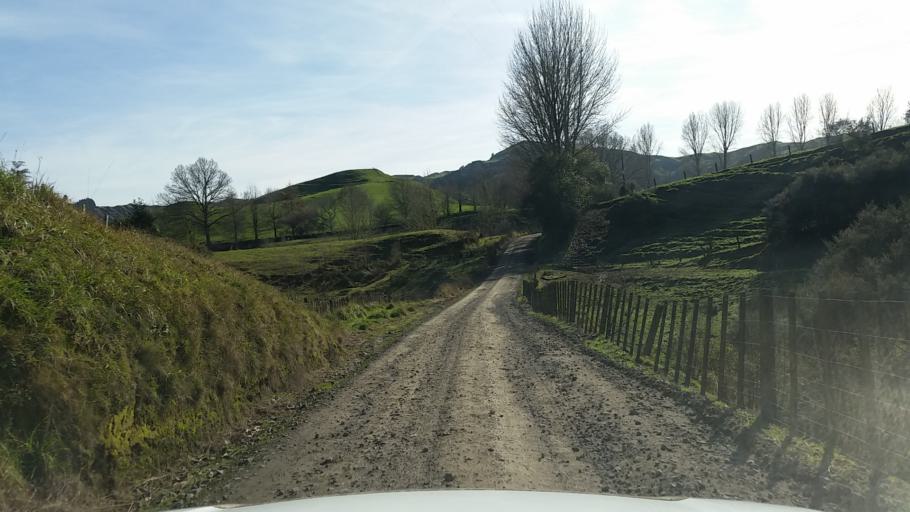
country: NZ
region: Taranaki
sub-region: South Taranaki District
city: Eltham
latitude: -39.3532
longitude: 174.5134
